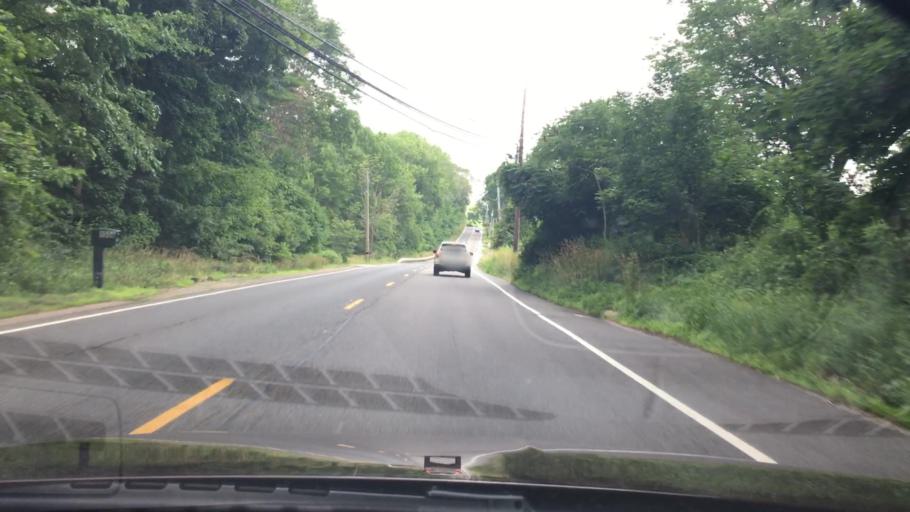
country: US
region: Connecticut
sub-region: Tolland County
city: Storrs
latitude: 41.8220
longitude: -72.2601
